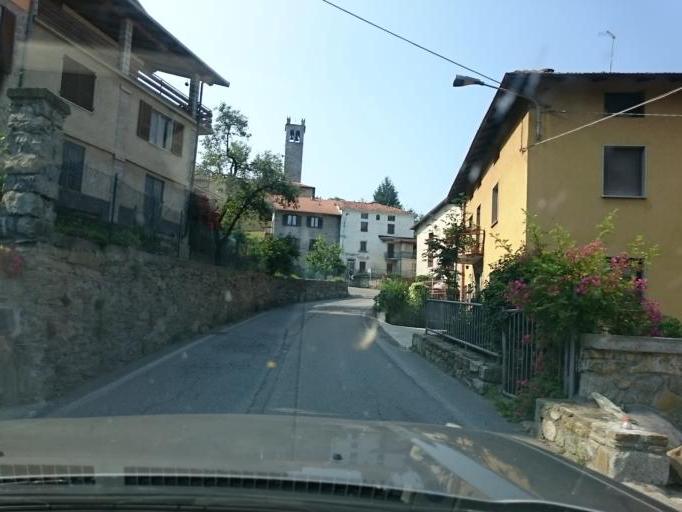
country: IT
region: Lombardy
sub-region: Provincia di Brescia
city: Cimbergo
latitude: 46.0221
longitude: 10.3640
